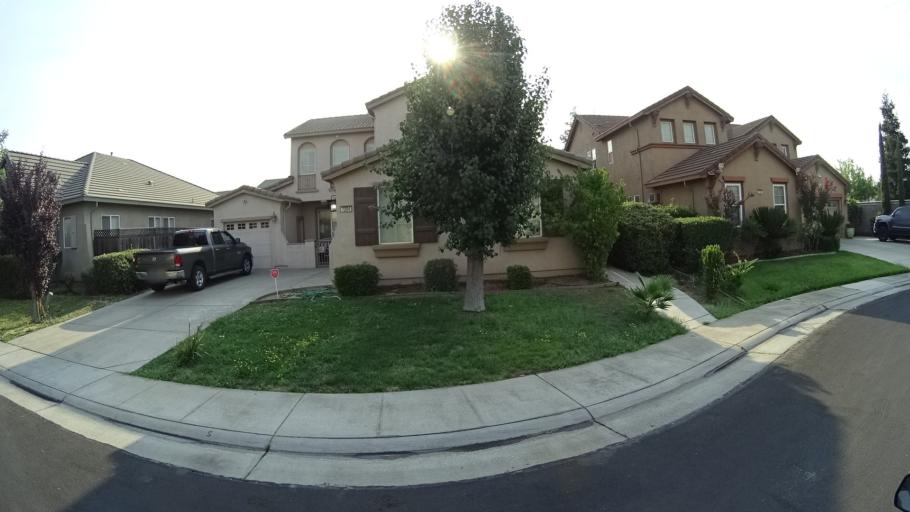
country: US
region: California
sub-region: Sacramento County
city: Laguna
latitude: 38.3852
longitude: -121.4198
